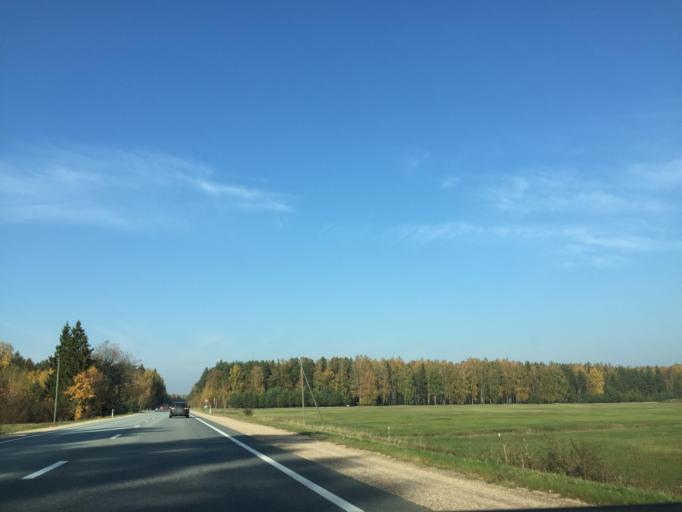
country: LV
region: Babite
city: Pinki
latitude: 56.8916
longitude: 23.9356
